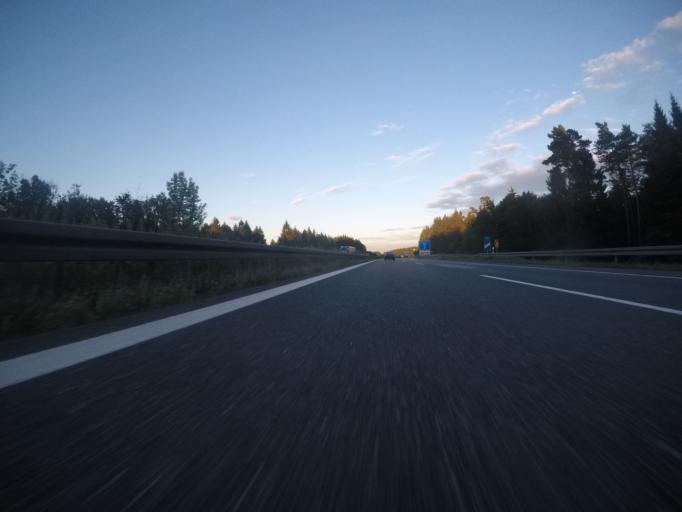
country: DE
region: Bavaria
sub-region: Upper Palatinate
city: Illschwang
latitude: 49.4253
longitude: 11.6797
